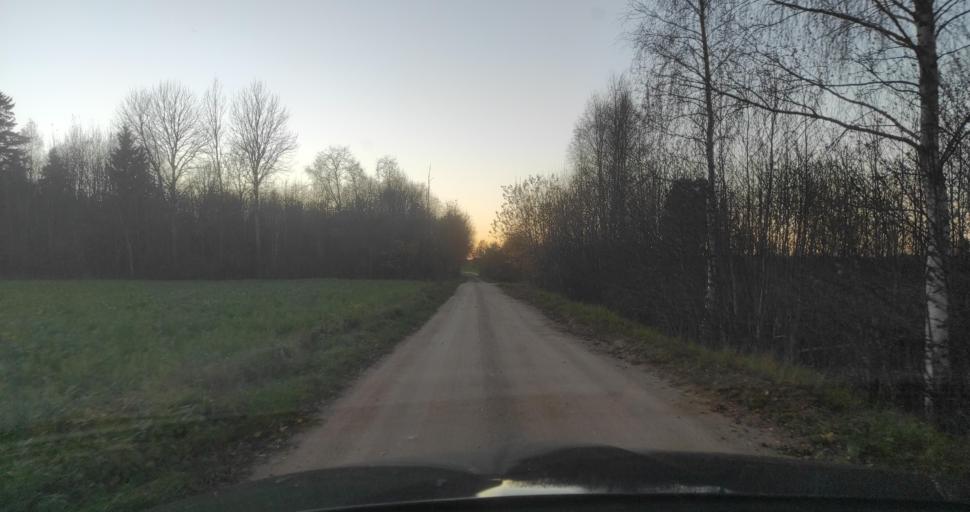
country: LV
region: Saldus Rajons
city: Saldus
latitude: 56.8033
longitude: 22.2764
